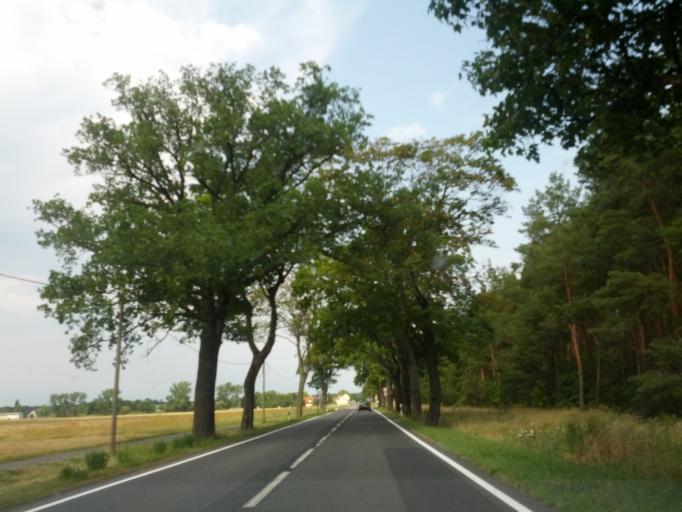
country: DE
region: Brandenburg
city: Nauen
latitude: 52.6766
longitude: 12.9327
